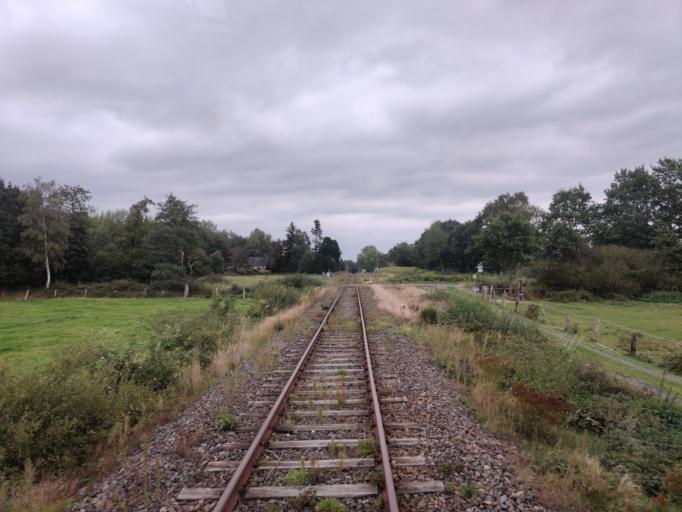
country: DE
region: Lower Saxony
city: Gnarrenburg
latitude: 53.4122
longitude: 9.0125
